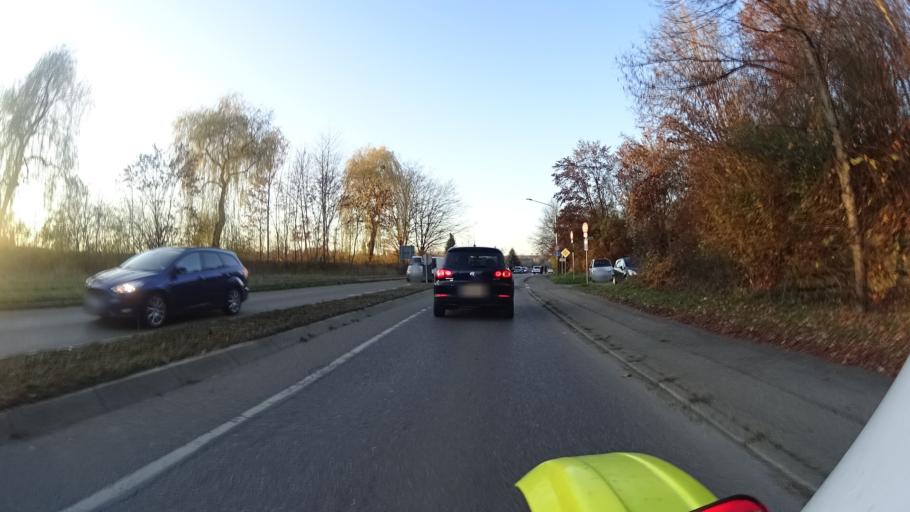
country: DE
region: Baden-Wuerttemberg
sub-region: Regierungsbezirk Stuttgart
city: Schlat
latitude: 48.6710
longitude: 9.6919
